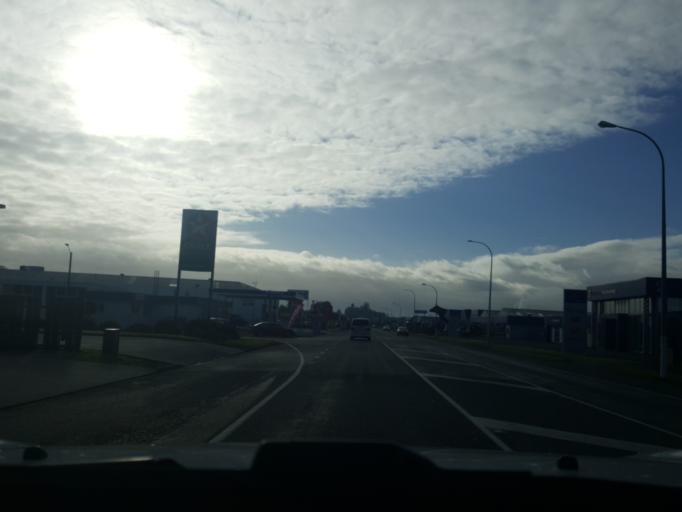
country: NZ
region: Waikato
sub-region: Waipa District
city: Cambridge
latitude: -37.6607
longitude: 175.5203
